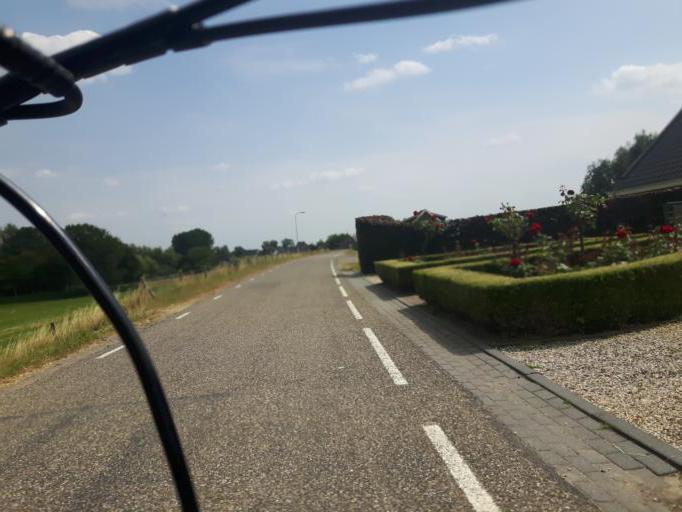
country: NL
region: Gelderland
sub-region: Gemeente Zaltbommel
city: Nederhemert
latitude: 51.8197
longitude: 5.1416
